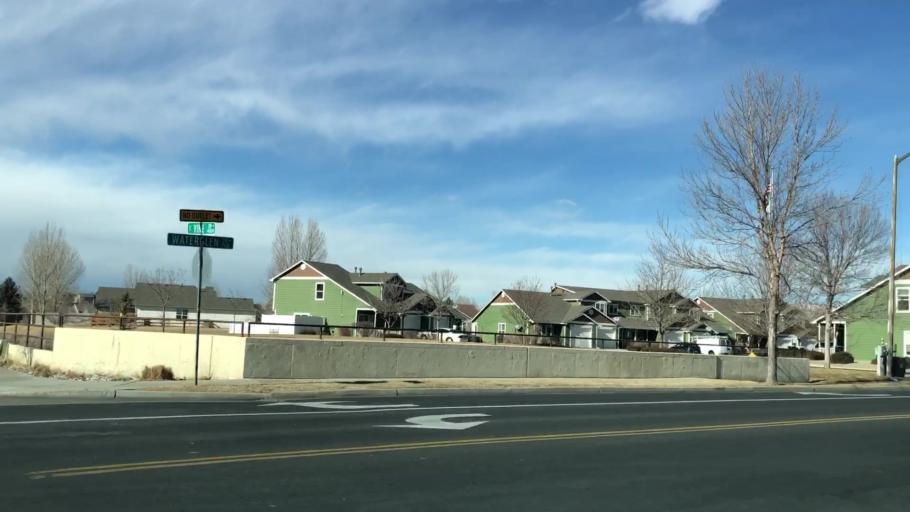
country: US
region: Colorado
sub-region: Larimer County
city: Fort Collins
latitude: 40.5959
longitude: -105.0055
